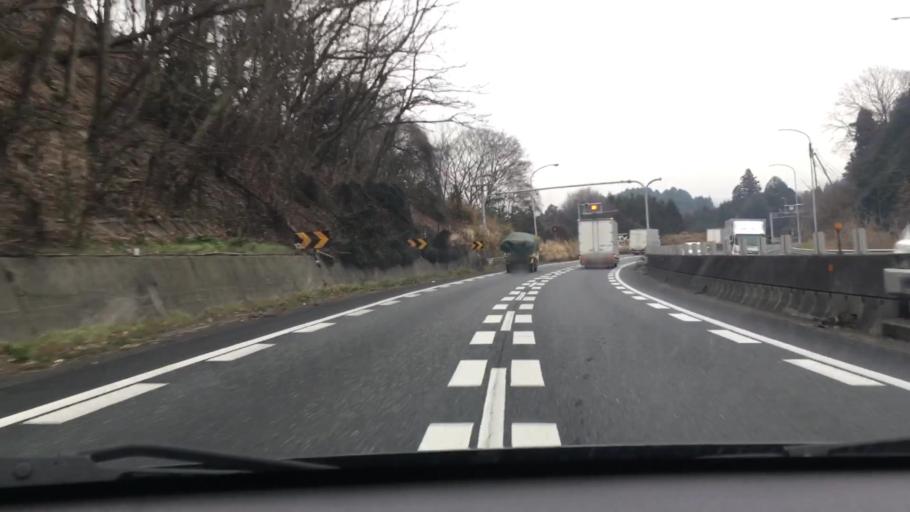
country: JP
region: Mie
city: Nabari
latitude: 34.6904
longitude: 136.0489
